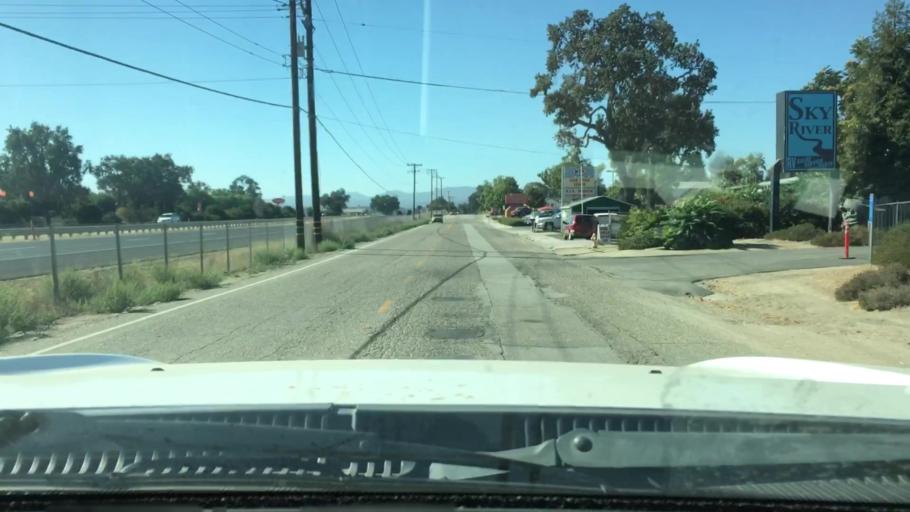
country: US
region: California
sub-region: San Luis Obispo County
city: Templeton
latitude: 35.5805
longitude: -120.6972
